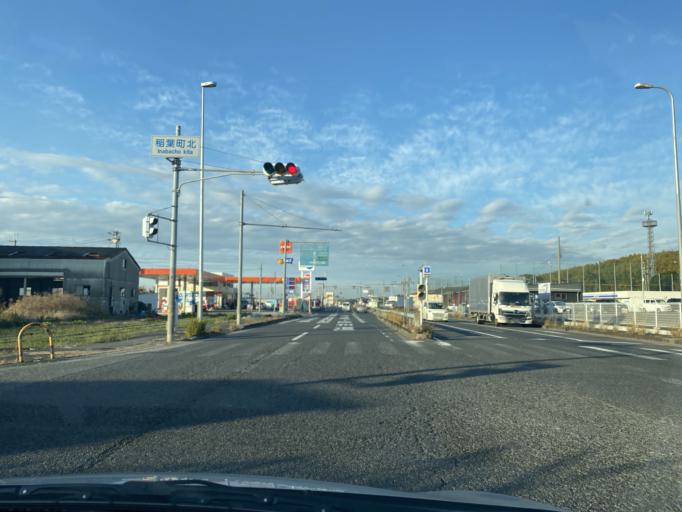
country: JP
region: Osaka
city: Izumi
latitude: 34.4364
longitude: 135.4395
